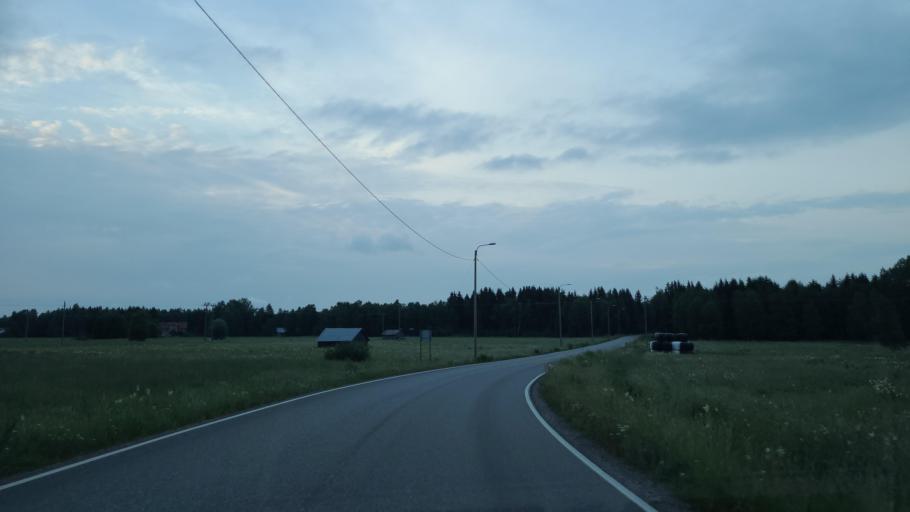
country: FI
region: Ostrobothnia
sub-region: Vaasa
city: Replot
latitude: 63.1974
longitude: 21.3070
